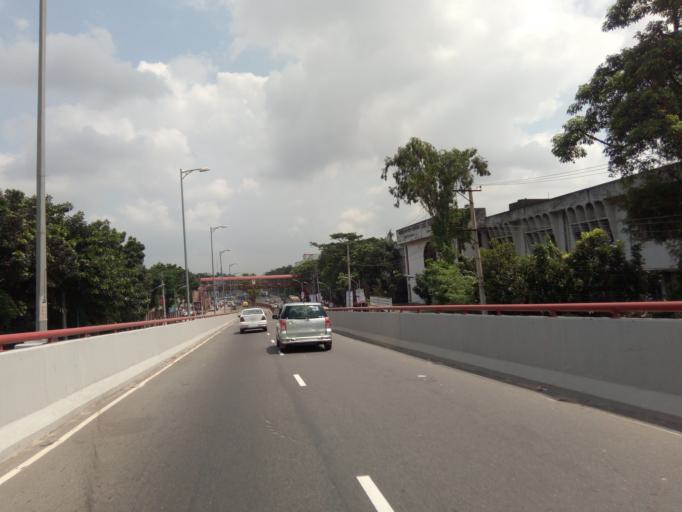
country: BD
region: Dhaka
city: Paltan
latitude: 23.7574
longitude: 90.3990
